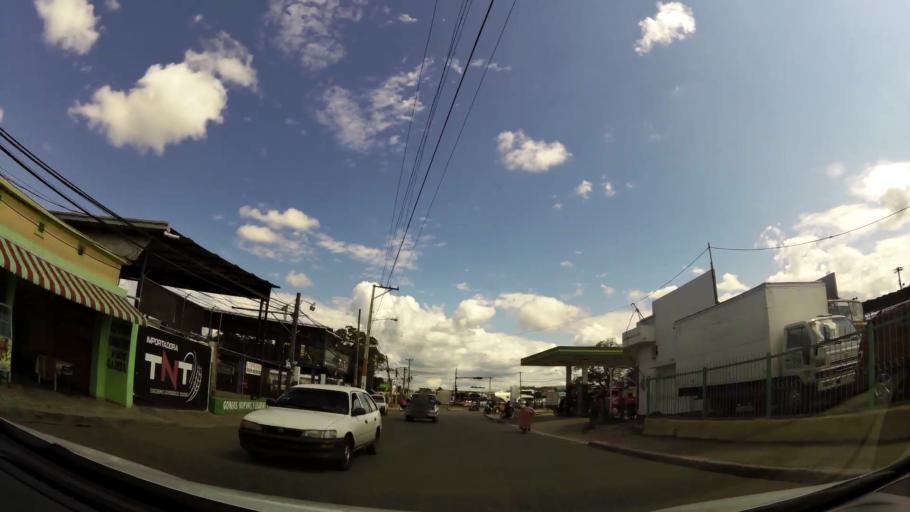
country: DO
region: La Vega
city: Concepcion de La Vega
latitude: 19.2368
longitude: -70.5337
